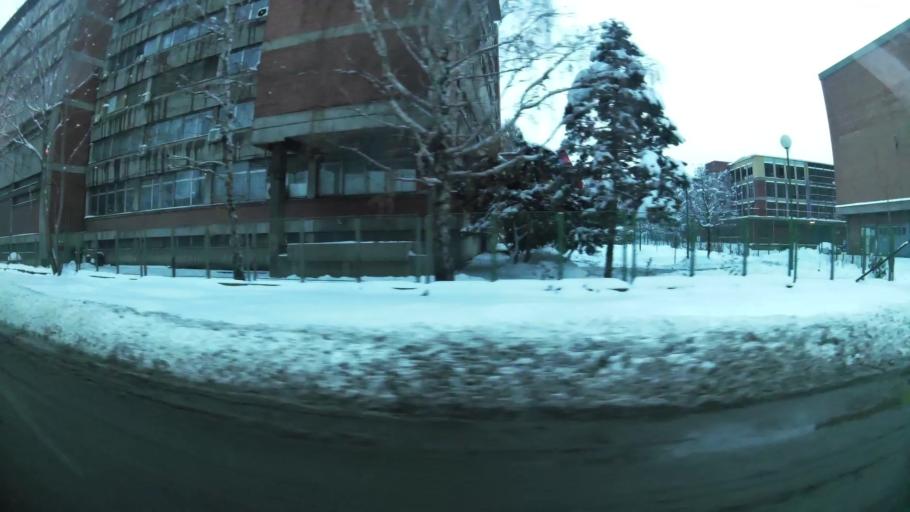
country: RS
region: Central Serbia
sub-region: Belgrade
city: Stari Grad
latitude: 44.8214
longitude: 20.4858
